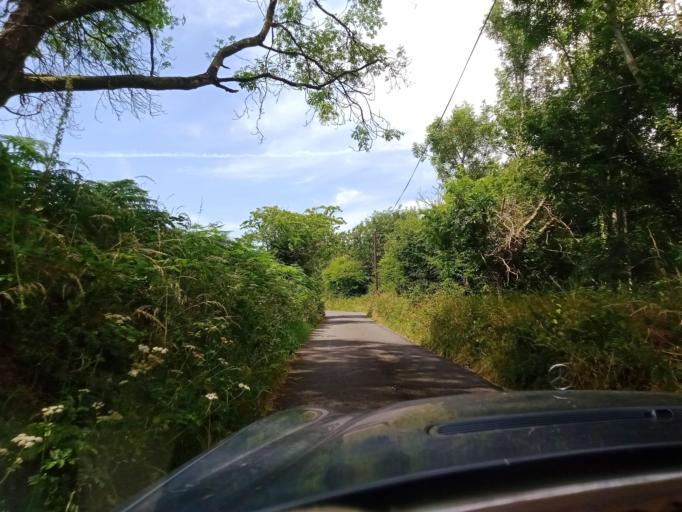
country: IE
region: Leinster
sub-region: Kilkenny
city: Mooncoin
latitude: 52.2569
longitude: -7.2115
